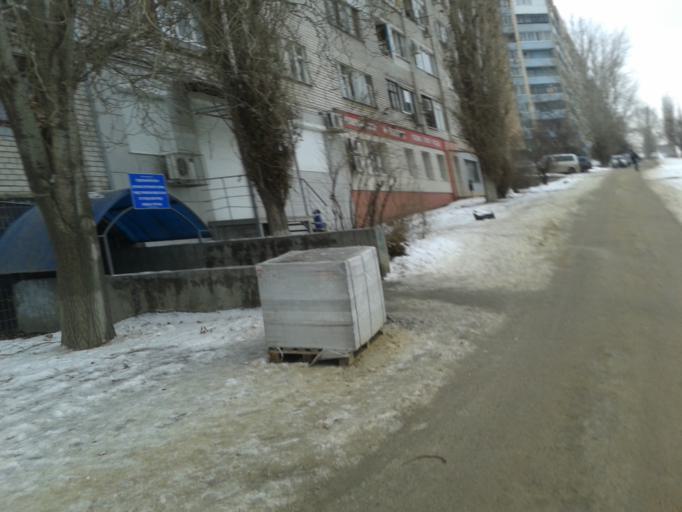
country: RU
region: Volgograd
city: Volgograd
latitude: 48.7254
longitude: 44.5249
